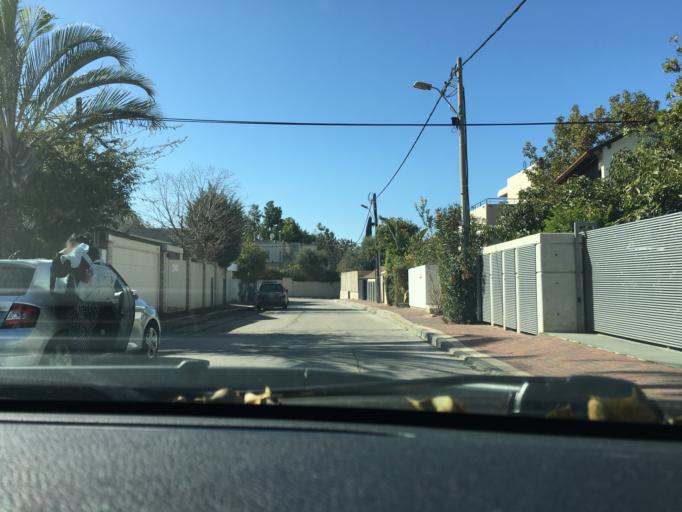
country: IL
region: Tel Aviv
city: Ramat HaSharon
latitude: 32.1490
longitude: 34.8335
